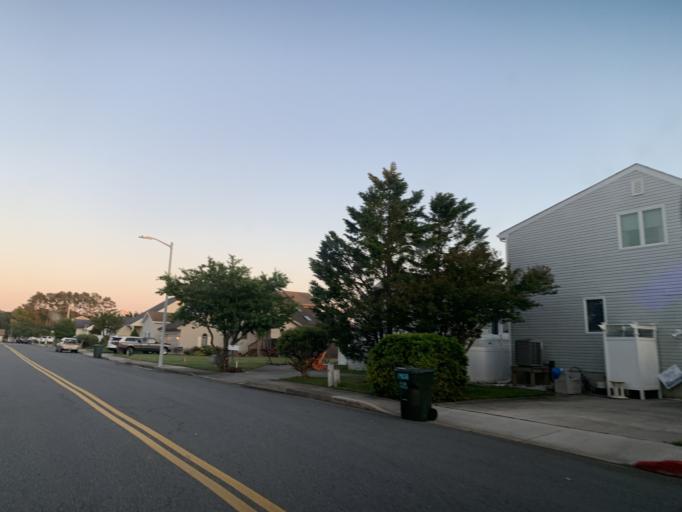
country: US
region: Delaware
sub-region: Sussex County
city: Bethany Beach
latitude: 38.4506
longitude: -75.0647
